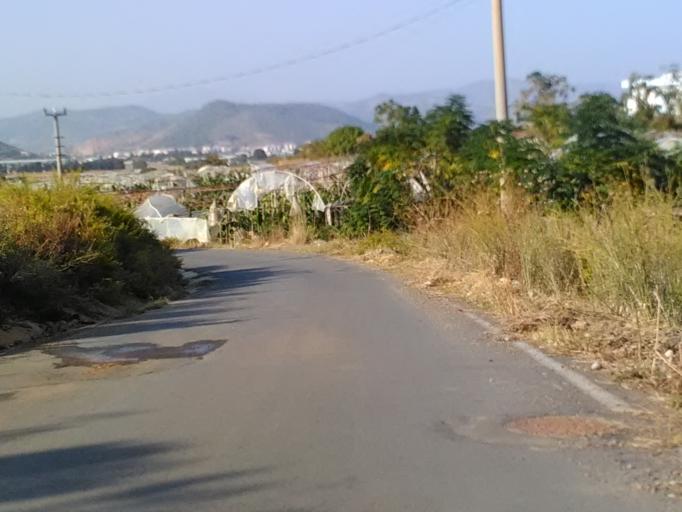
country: TR
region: Antalya
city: Gazipasa
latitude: 36.2345
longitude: 32.3004
